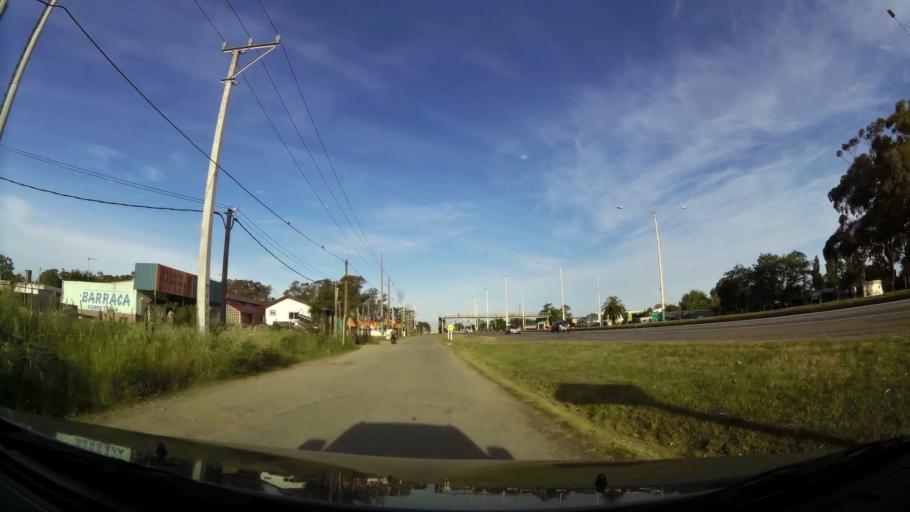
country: UY
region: Canelones
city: Atlantida
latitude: -34.7753
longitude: -55.8428
